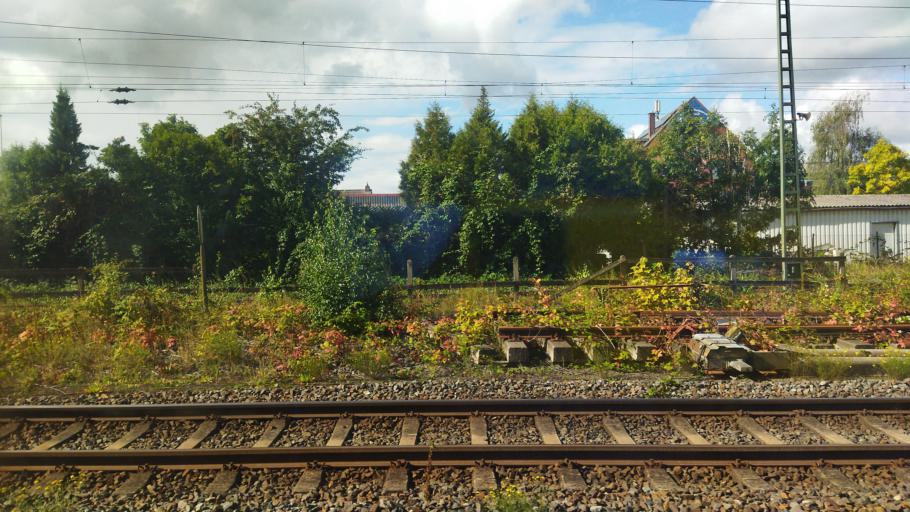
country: DE
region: Lower Saxony
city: Emden
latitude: 53.3680
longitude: 7.1951
